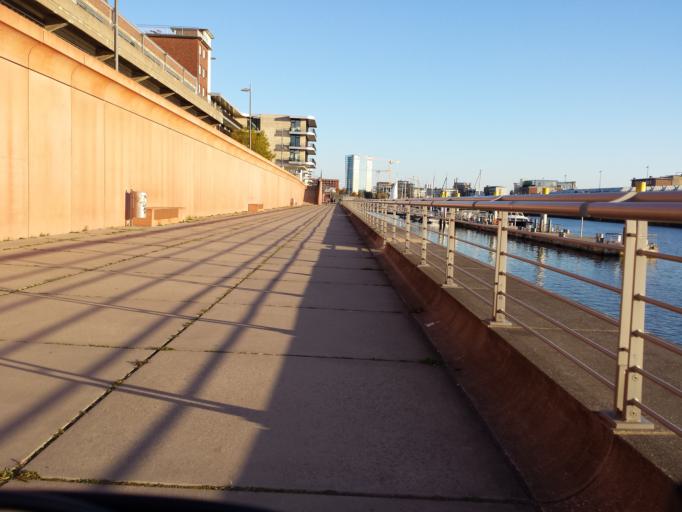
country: DE
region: Bremen
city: Bremen
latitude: 53.0894
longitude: 8.7754
